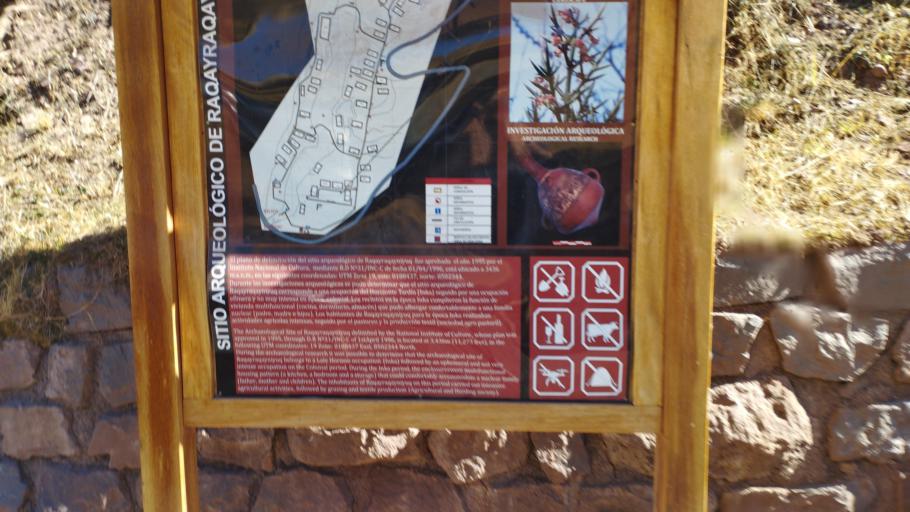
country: PE
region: Cusco
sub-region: Provincia de Cusco
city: Saylla
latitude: -13.5307
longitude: -71.8788
